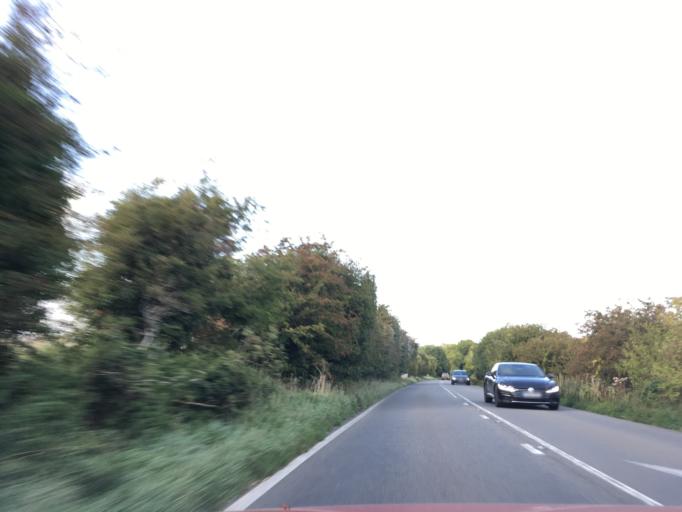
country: GB
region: England
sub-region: Gloucestershire
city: Bourton on the Water
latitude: 51.8646
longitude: -1.7977
